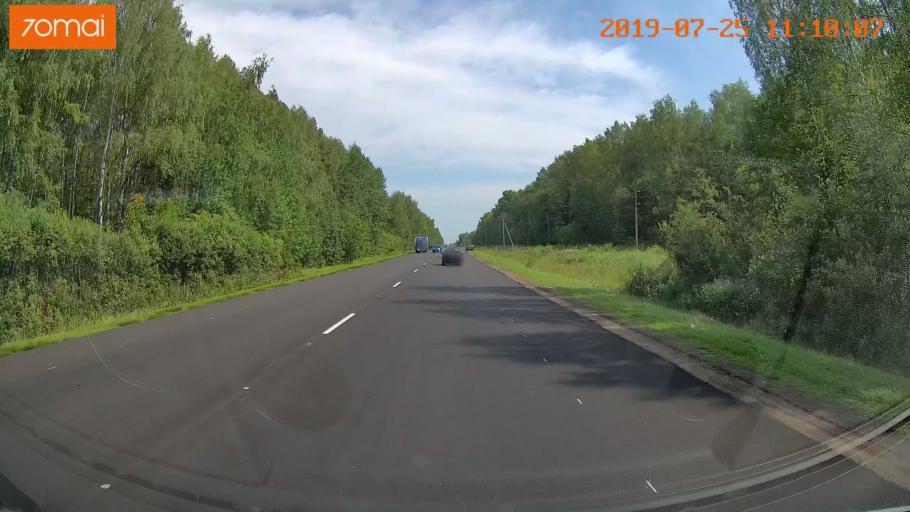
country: RU
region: Ivanovo
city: Furmanov
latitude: 57.2967
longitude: 41.1877
